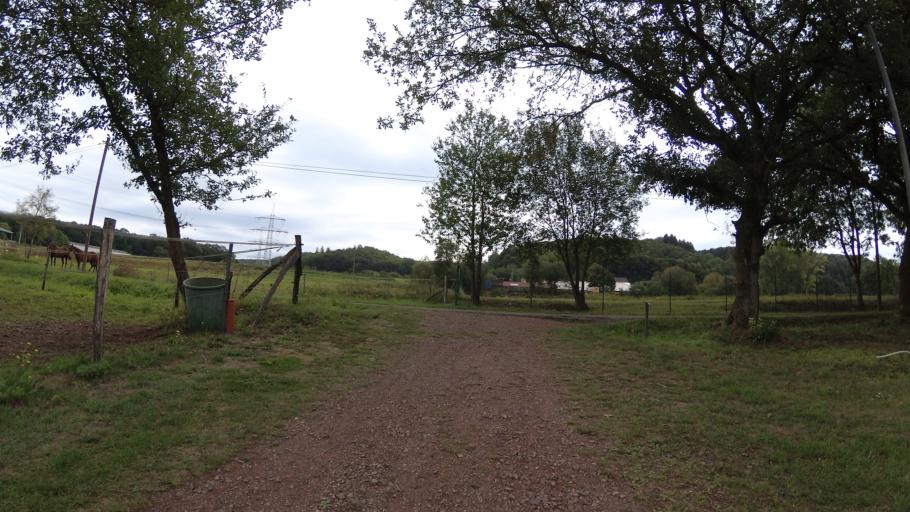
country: DE
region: Saarland
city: Wadern
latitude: 49.5207
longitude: 6.8907
